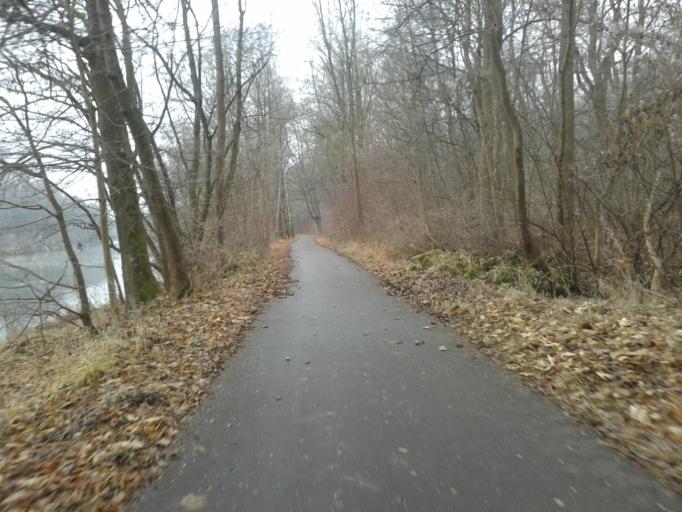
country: DE
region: Bavaria
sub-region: Swabia
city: Neu-Ulm
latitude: 48.4290
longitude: 10.0367
